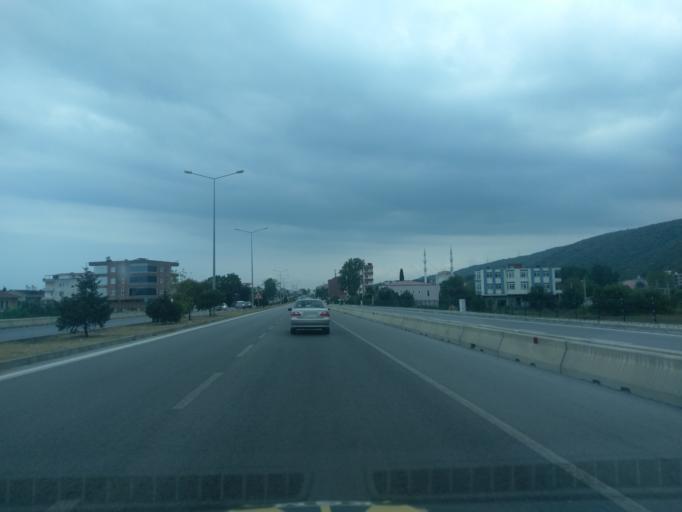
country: TR
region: Samsun
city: Taflan
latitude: 41.4056
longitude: 36.1824
